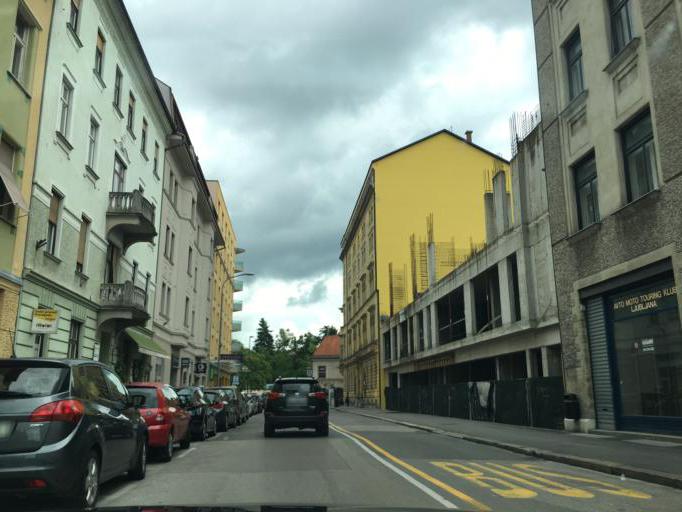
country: SI
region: Ljubljana
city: Ljubljana
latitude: 46.0538
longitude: 14.5071
